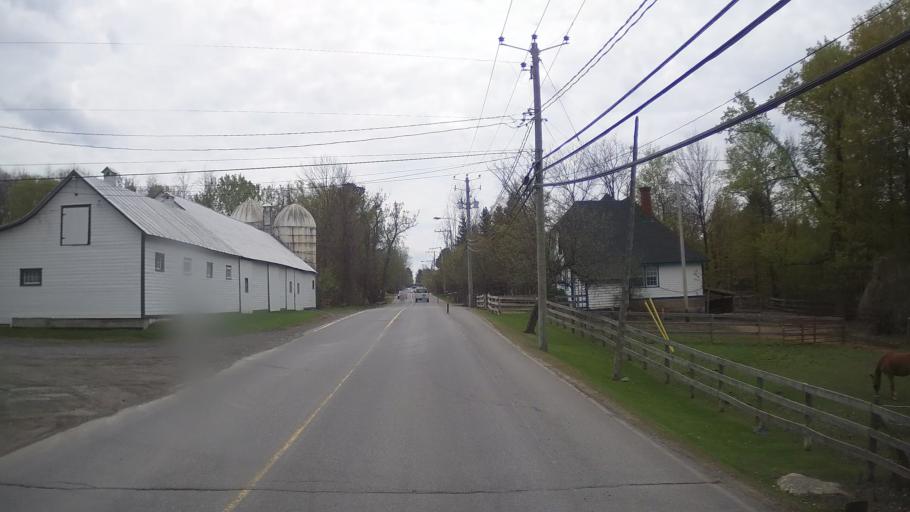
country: CA
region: Quebec
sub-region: Monteregie
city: Hudson
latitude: 45.4415
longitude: -74.1704
